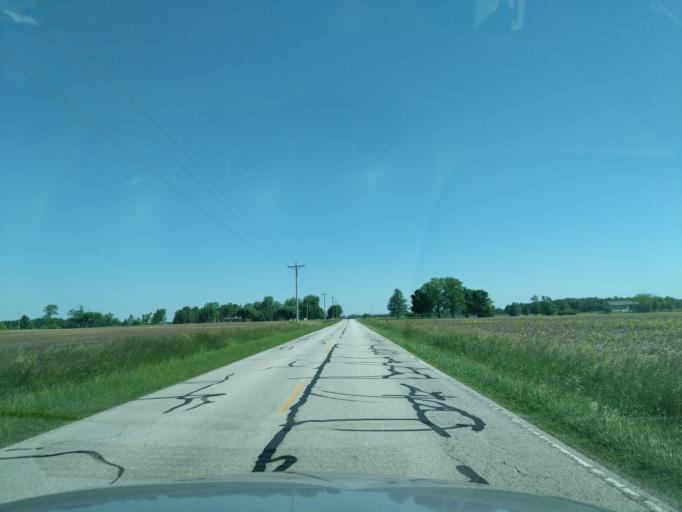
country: US
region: Indiana
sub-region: Huntington County
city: Warren
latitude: 40.6941
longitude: -85.5068
